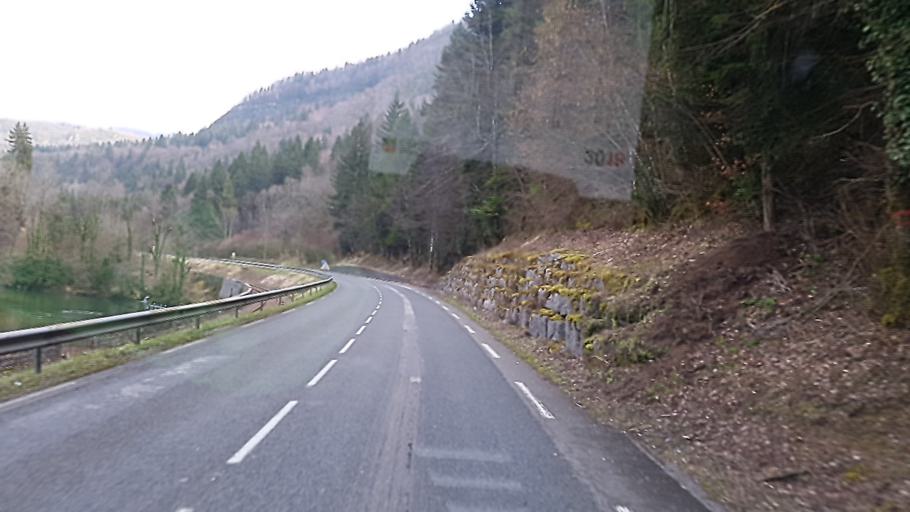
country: FR
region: Franche-Comte
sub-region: Departement du Jura
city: Lavans-les-Saint-Claude
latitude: 46.3502
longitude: 5.7485
